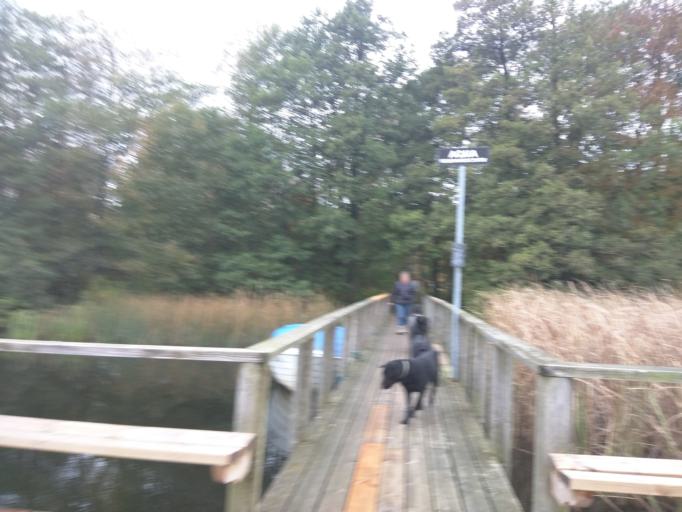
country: DK
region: Central Jutland
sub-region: Silkeborg Kommune
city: Virklund
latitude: 56.1515
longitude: 9.5644
